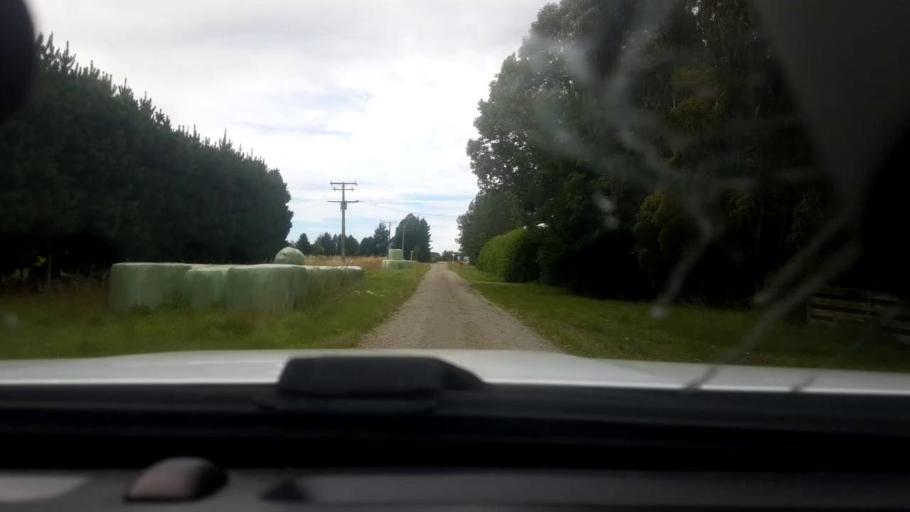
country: NZ
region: Canterbury
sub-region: Timaru District
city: Pleasant Point
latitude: -44.1345
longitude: 171.2885
